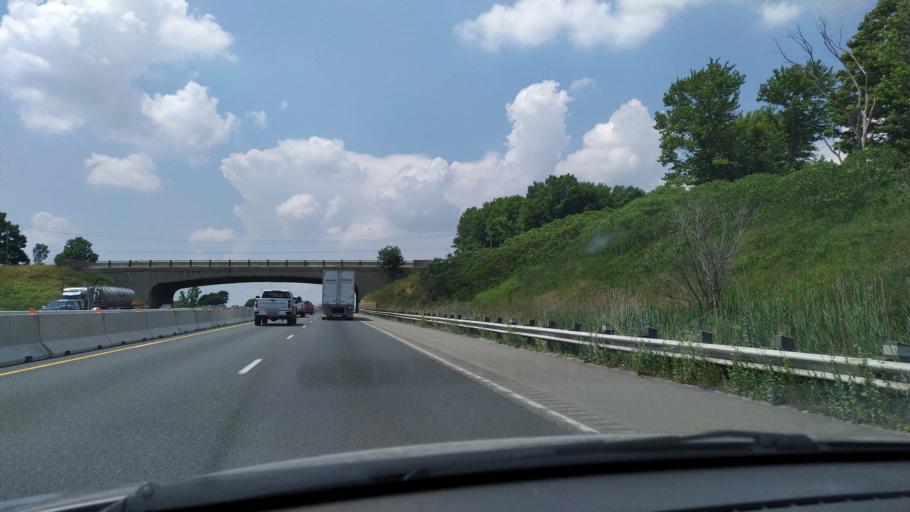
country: CA
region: Ontario
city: Dorchester
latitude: 42.9588
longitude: -81.0593
